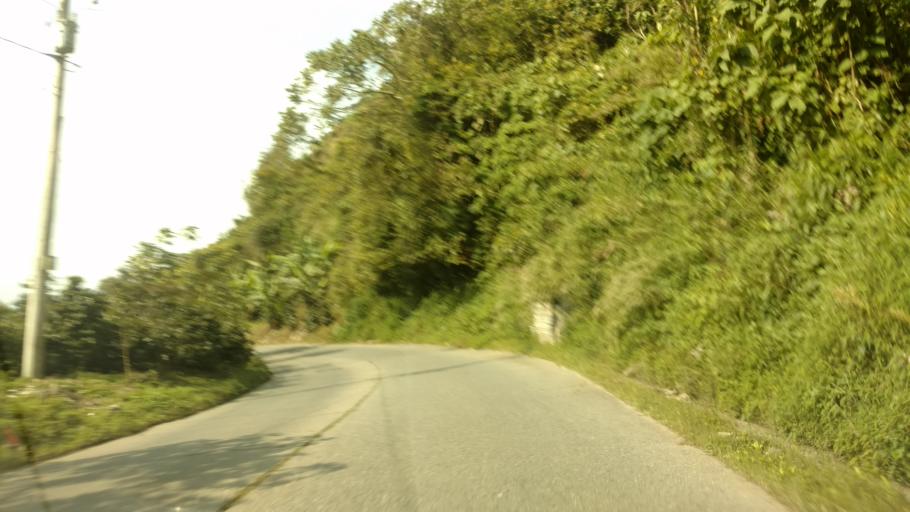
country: CO
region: Caldas
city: Manizales
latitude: 5.0845
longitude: -75.5177
